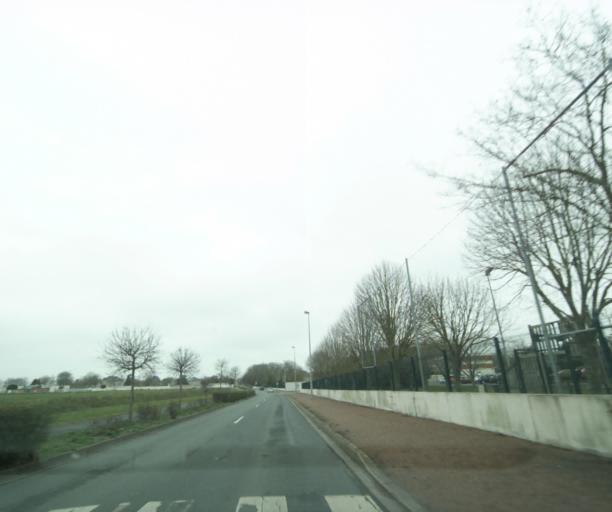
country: FR
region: Poitou-Charentes
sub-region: Departement de la Charente-Maritime
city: Puilboreau
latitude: 46.1743
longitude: -1.1290
